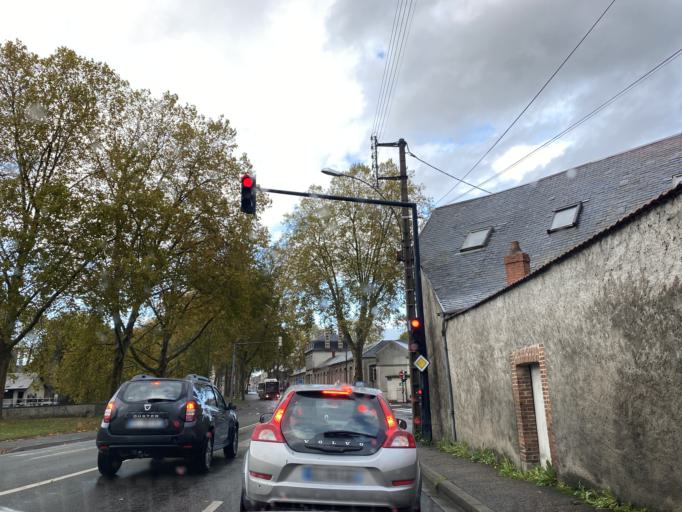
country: FR
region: Centre
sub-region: Departement du Cher
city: Bourges
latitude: 47.0806
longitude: 2.3895
